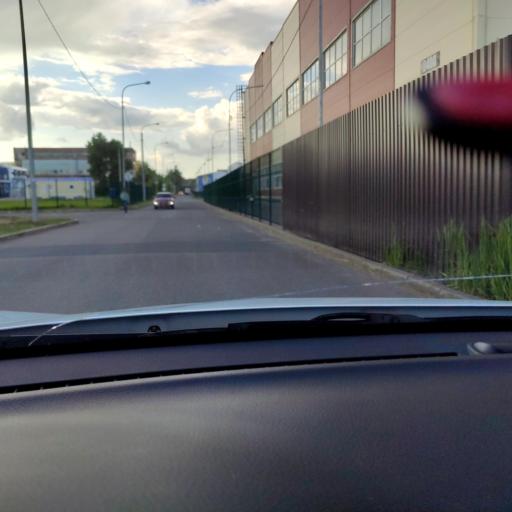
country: RU
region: Tatarstan
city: Staroye Arakchino
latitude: 55.8305
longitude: 49.0369
